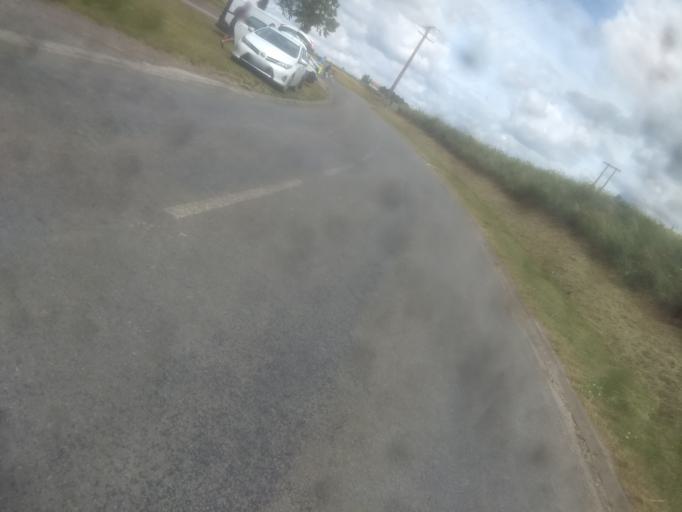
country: FR
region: Nord-Pas-de-Calais
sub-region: Departement du Pas-de-Calais
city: Duisans
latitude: 50.3072
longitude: 2.6641
